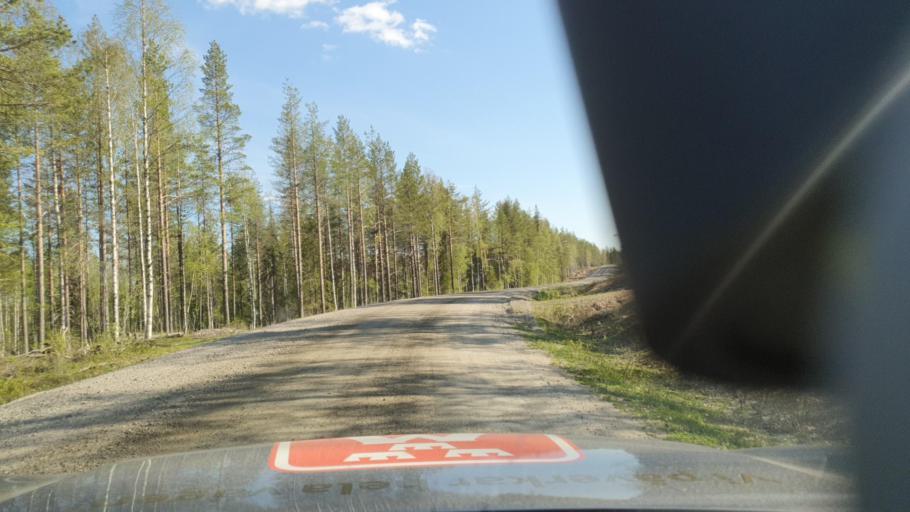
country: SE
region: Norrbotten
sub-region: Bodens Kommun
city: Boden
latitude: 66.4596
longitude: 21.8671
